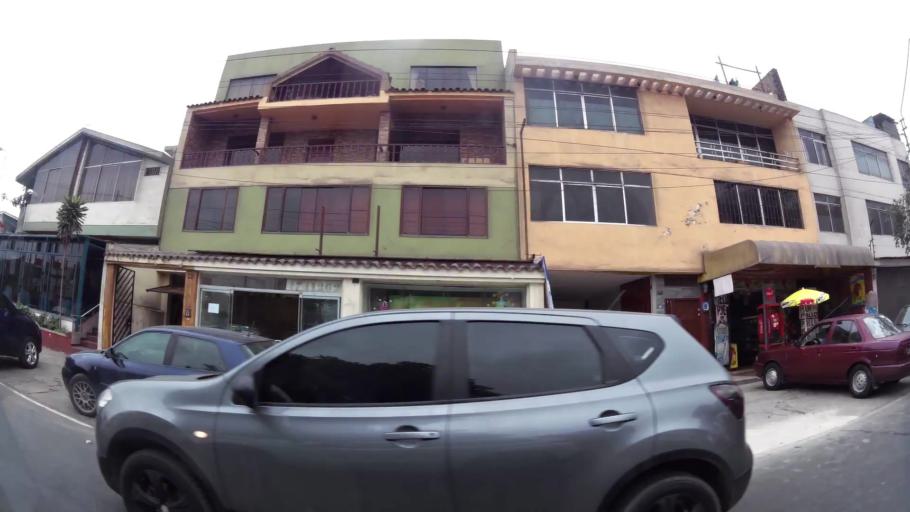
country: PE
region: Lima
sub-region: Lima
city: San Luis
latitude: -12.0761
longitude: -76.9953
